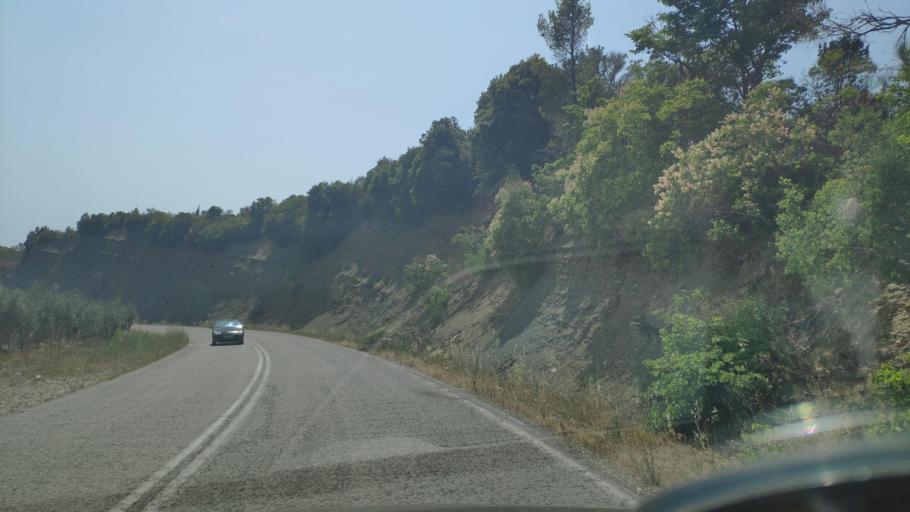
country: GR
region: Epirus
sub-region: Nomos Artas
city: Peta
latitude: 39.1860
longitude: 21.0970
